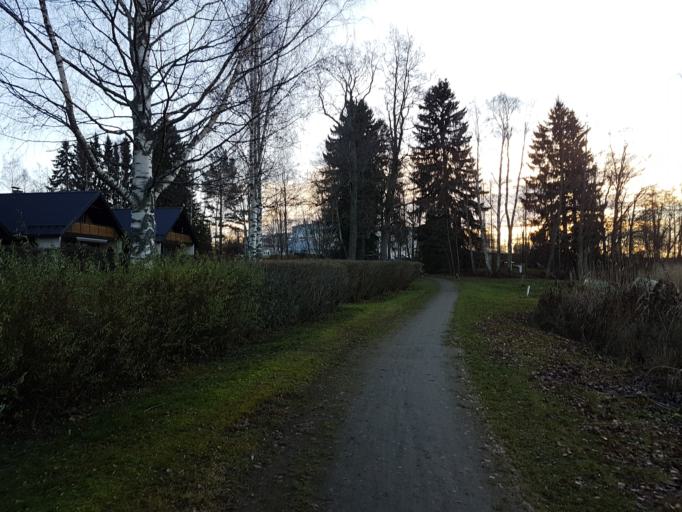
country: FI
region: Northern Savo
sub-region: Kuopio
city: Kuopio
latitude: 62.9347
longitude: 27.6302
